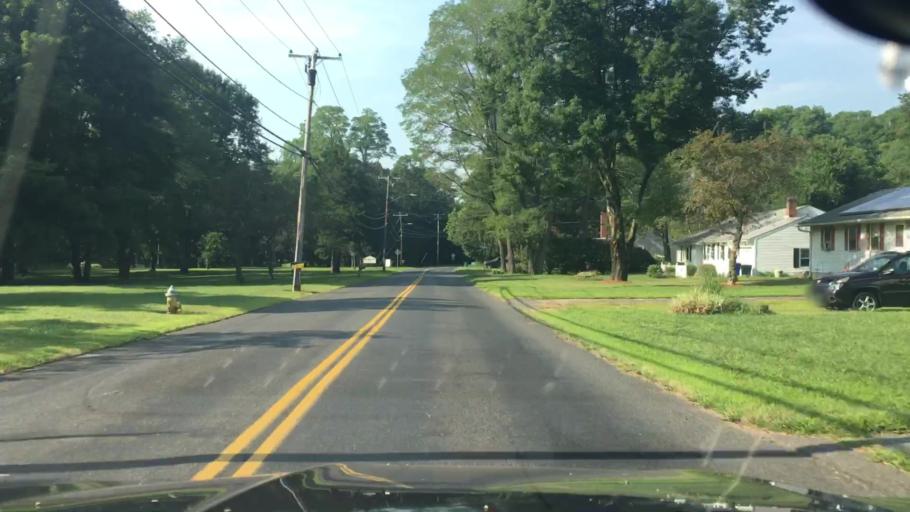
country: US
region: Connecticut
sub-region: Hartford County
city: South Windsor
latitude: 41.8626
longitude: -72.5769
